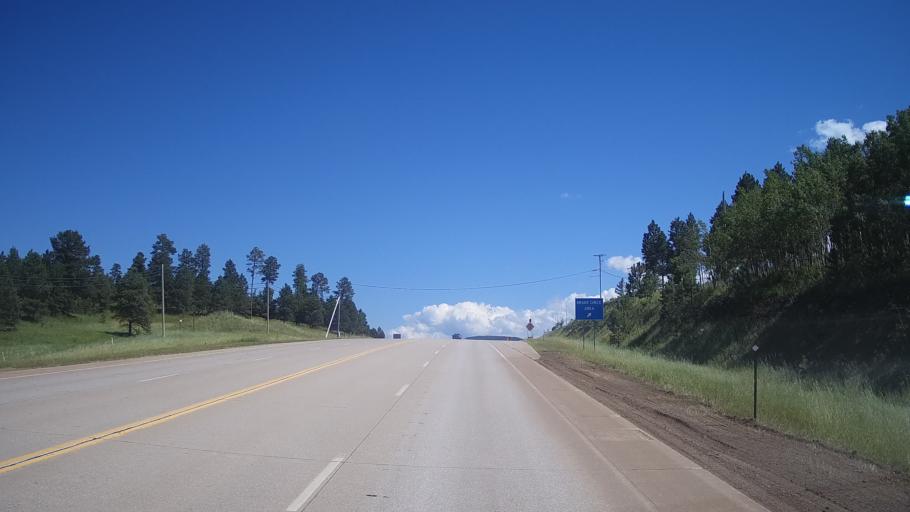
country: US
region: South Dakota
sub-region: Lawrence County
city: Deadwood
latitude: 44.3982
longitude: -103.7181
